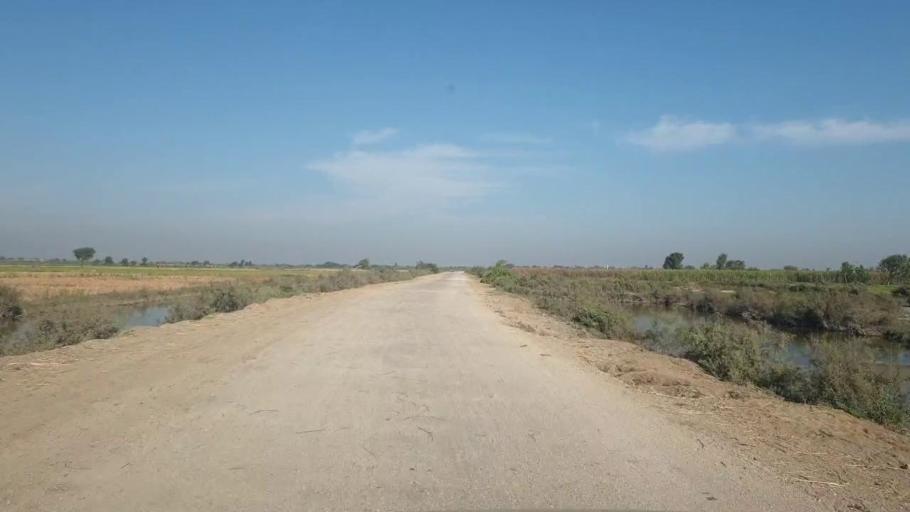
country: PK
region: Sindh
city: Talhar
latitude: 24.9165
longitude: 68.8033
